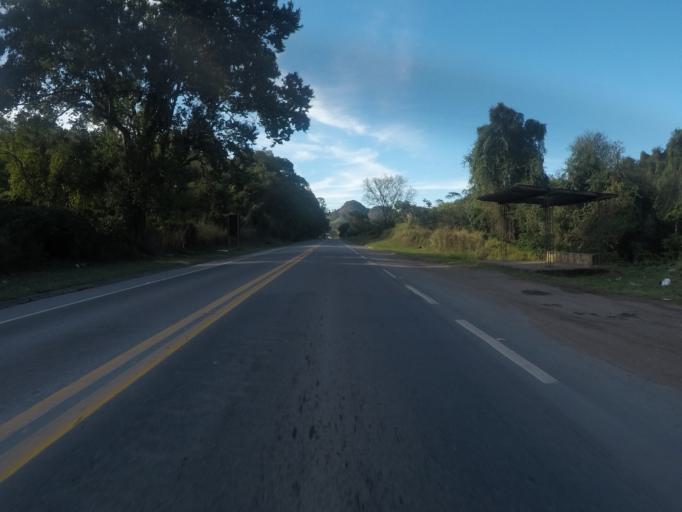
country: BR
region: Espirito Santo
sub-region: Fundao
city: Fundao
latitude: -19.8782
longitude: -40.4162
